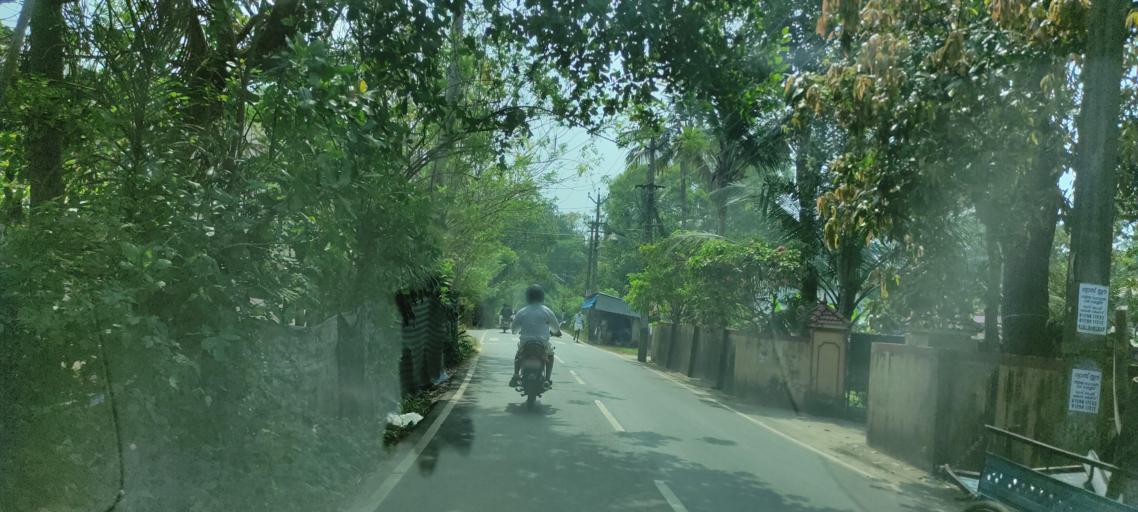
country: IN
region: Kerala
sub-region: Alappuzha
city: Alleppey
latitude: 9.5480
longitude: 76.3328
